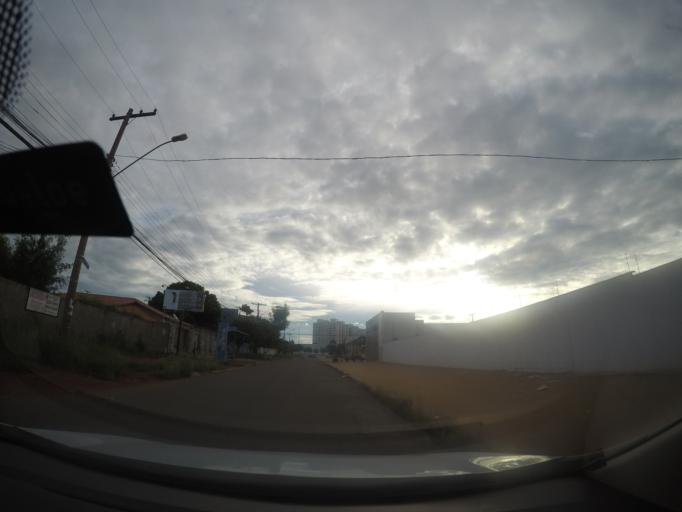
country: BR
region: Goias
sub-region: Goiania
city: Goiania
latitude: -16.6509
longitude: -49.3320
